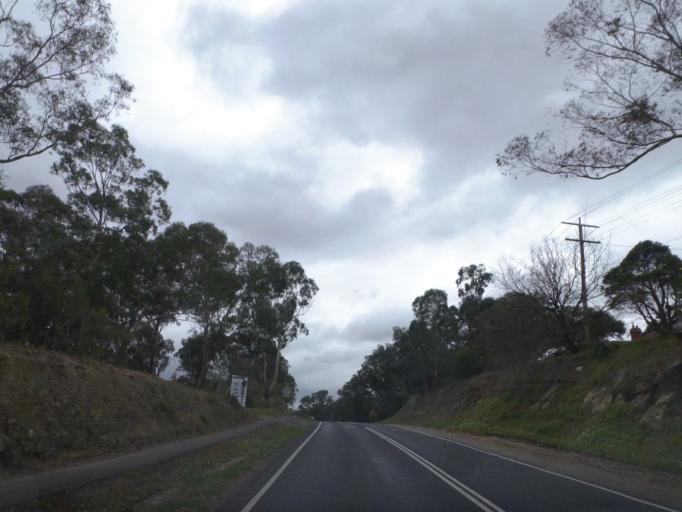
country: AU
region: Victoria
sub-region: Nillumbik
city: North Warrandyte
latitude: -37.7459
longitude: 145.2106
